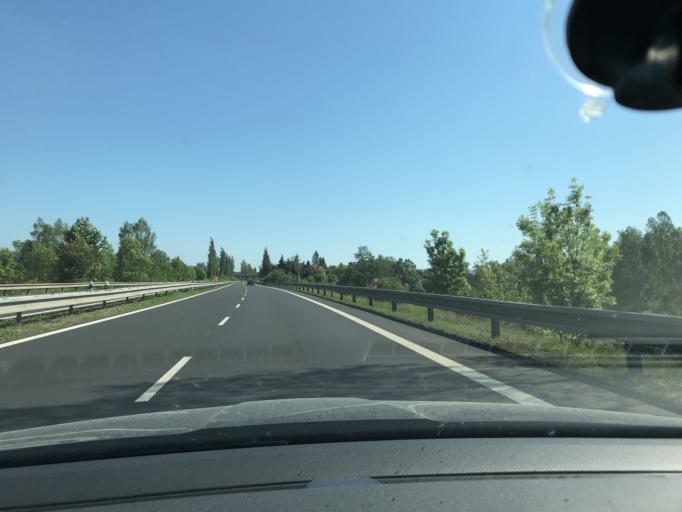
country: CZ
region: Karlovarsky
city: Sadov
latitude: 50.2670
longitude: 12.9298
